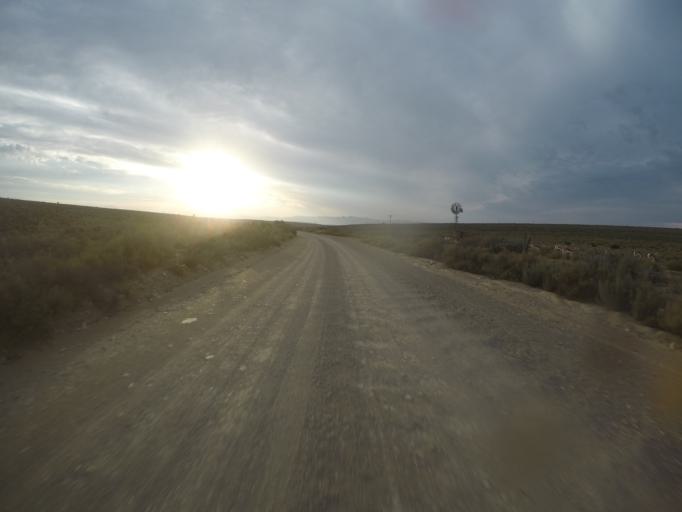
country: ZA
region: Eastern Cape
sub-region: Cacadu District Municipality
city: Willowmore
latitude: -33.5803
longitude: 23.1799
